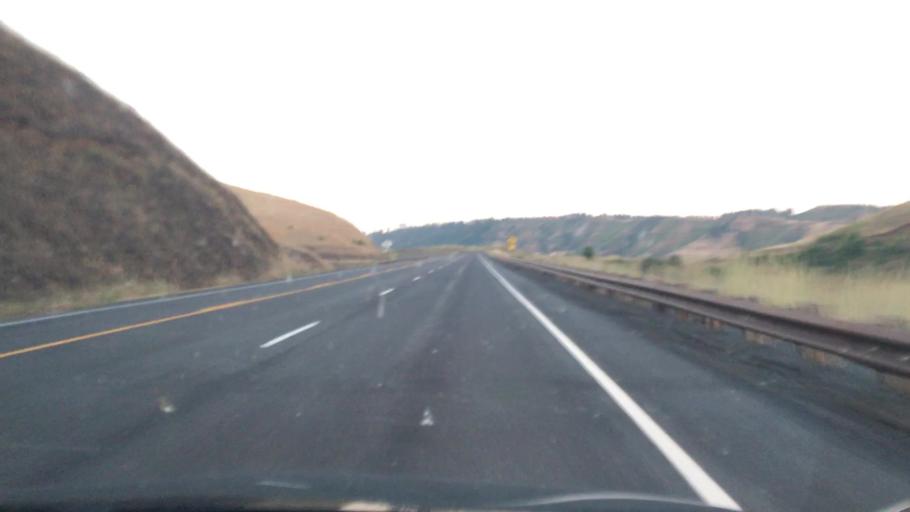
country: US
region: Idaho
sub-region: Idaho County
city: Grangeville
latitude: 45.8285
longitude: -116.2510
